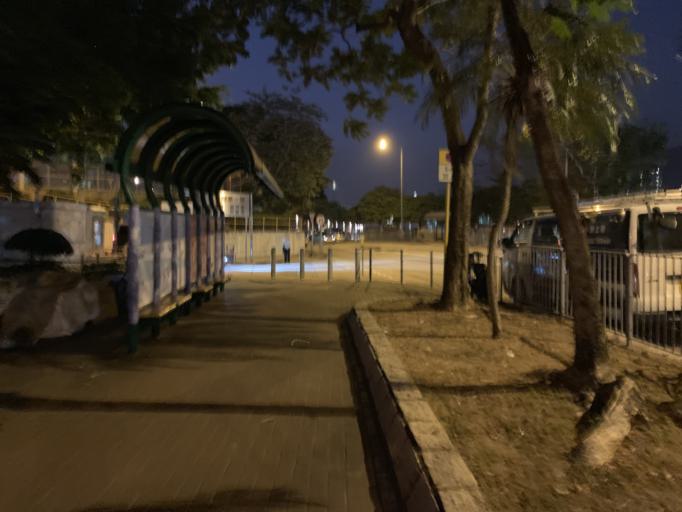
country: HK
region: Tsuen Wan
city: Tsuen Wan
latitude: 22.3623
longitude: 114.1010
